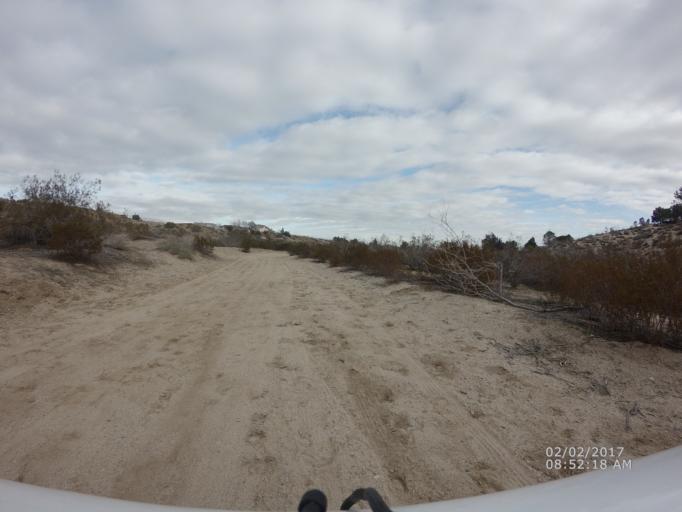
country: US
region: California
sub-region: Los Angeles County
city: Littlerock
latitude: 34.5287
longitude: -118.0325
